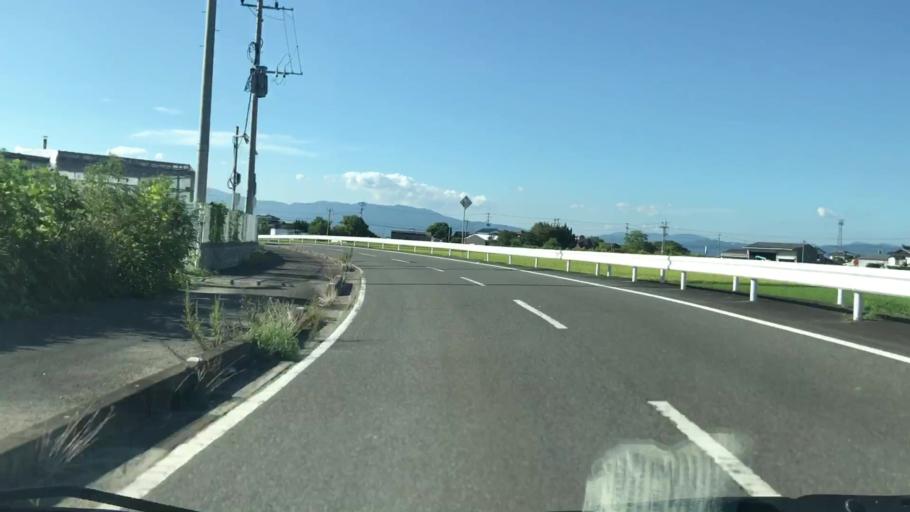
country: JP
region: Saga Prefecture
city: Saga-shi
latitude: 33.1884
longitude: 130.2893
